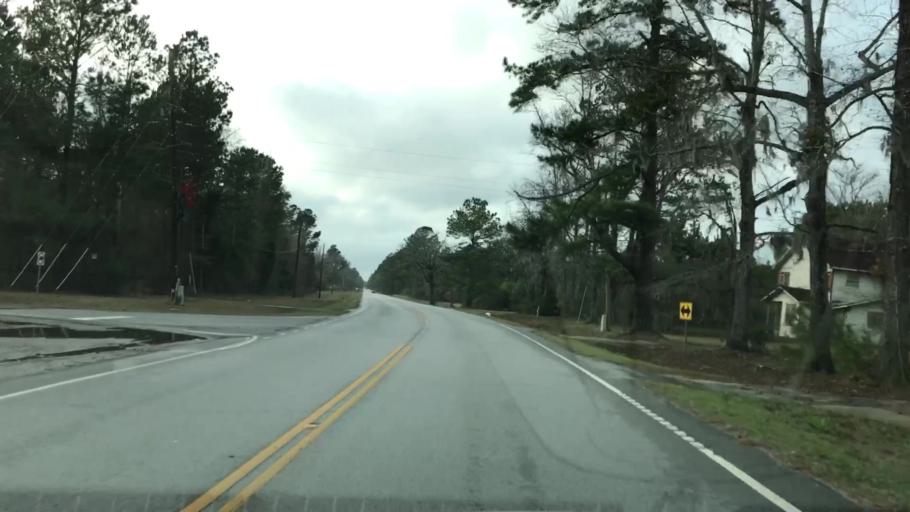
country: US
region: South Carolina
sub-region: Williamsburg County
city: Andrews
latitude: 33.2872
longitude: -79.6983
